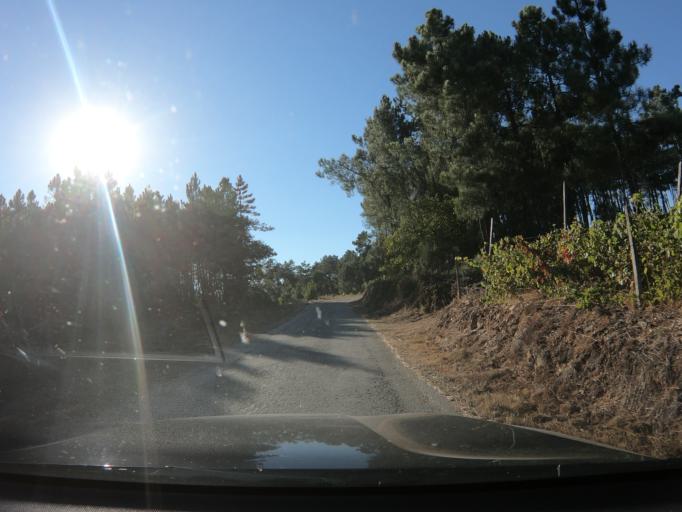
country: PT
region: Vila Real
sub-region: Sabrosa
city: Vilela
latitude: 41.2449
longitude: -7.6249
